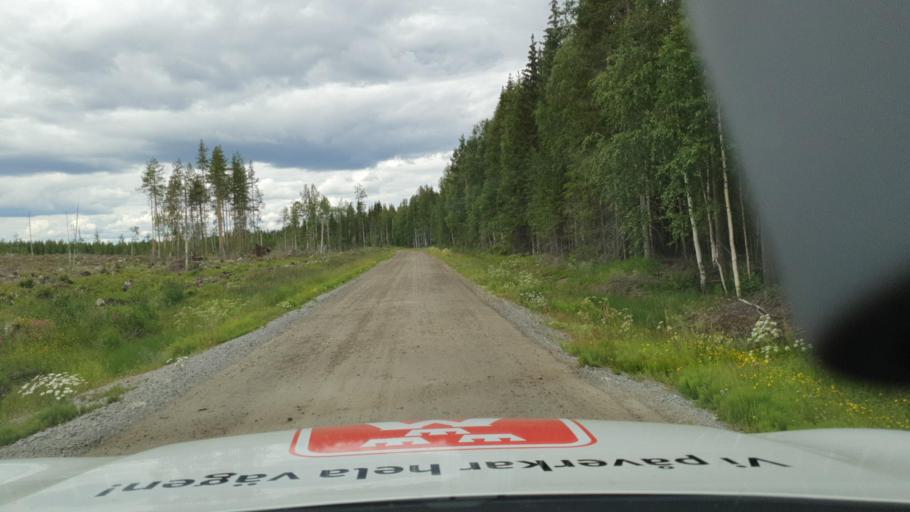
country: SE
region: Vaesterbotten
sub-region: Bjurholms Kommun
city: Bjurholm
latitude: 63.7869
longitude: 19.1119
